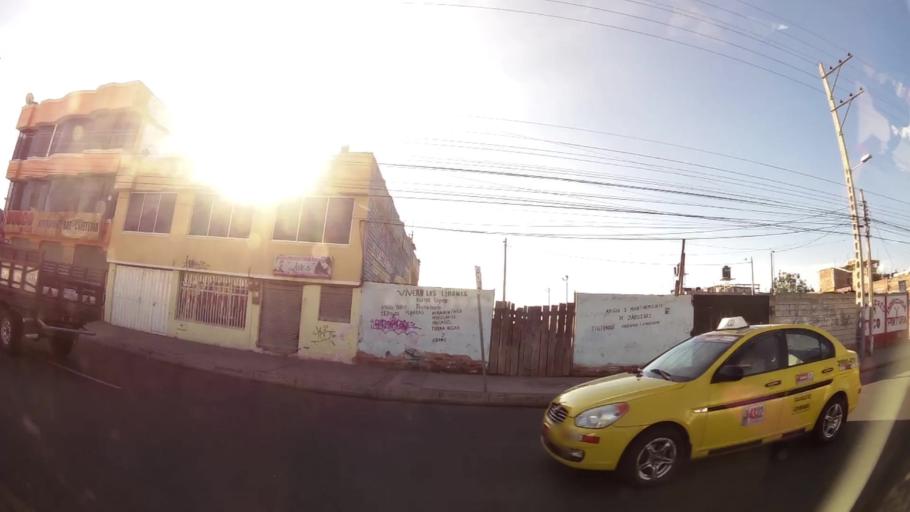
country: EC
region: Chimborazo
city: Riobamba
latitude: -1.6585
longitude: -78.6464
